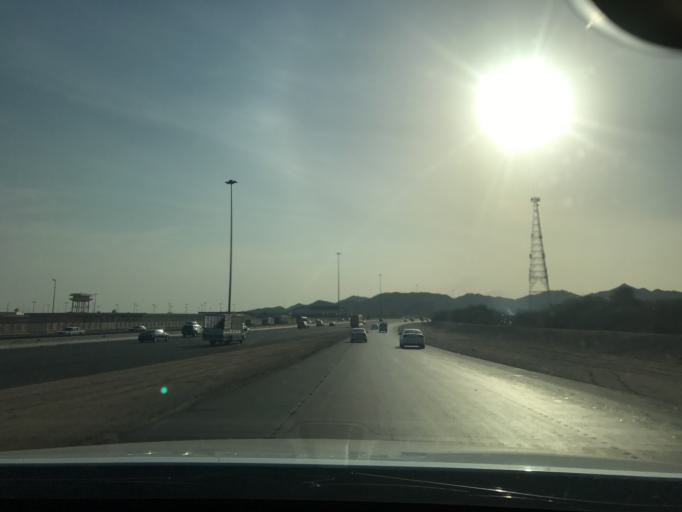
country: SA
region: Makkah
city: Jeddah
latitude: 21.3895
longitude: 39.4248
